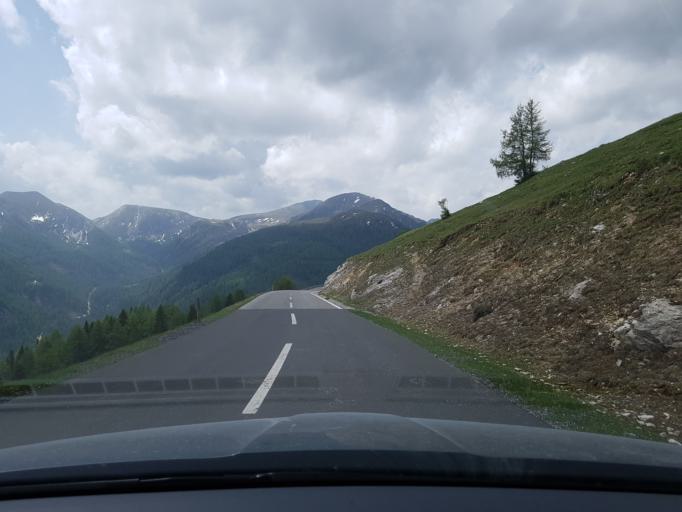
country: AT
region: Carinthia
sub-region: Politischer Bezirk Spittal an der Drau
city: Kleinkirchheim
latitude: 46.9291
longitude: 13.7589
